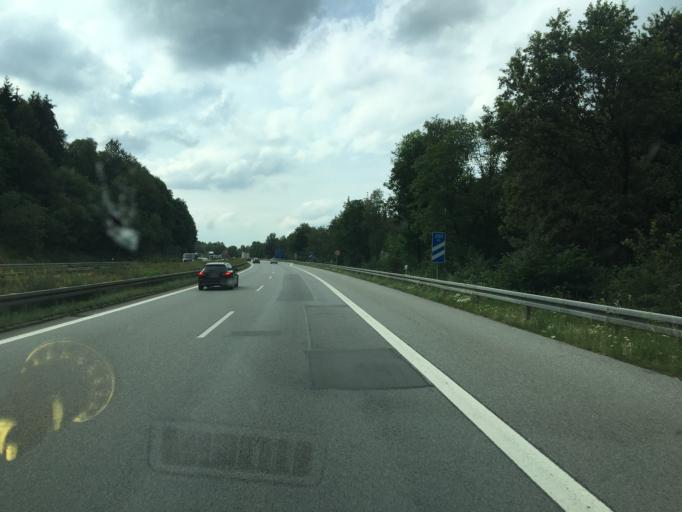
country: DE
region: Bavaria
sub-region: Lower Bavaria
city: Aussernzell
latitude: 48.6837
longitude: 13.2170
